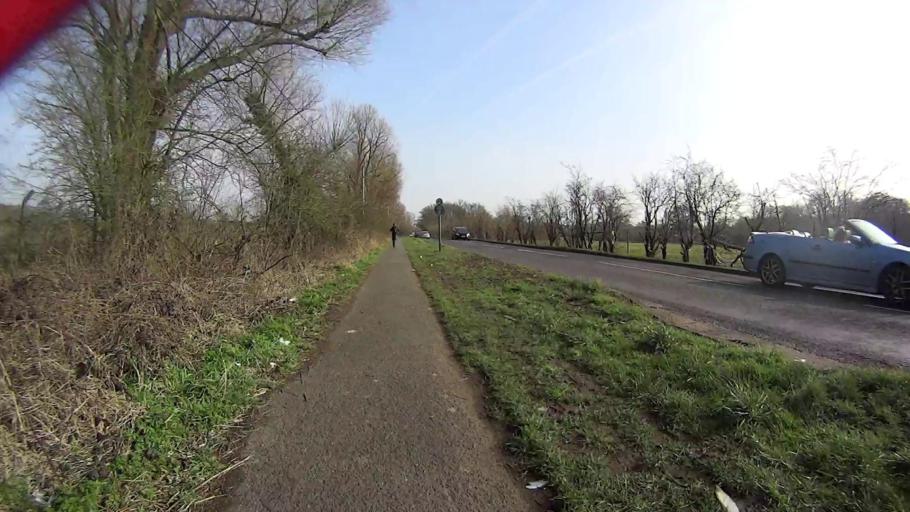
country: GB
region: England
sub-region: Surrey
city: Salfords
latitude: 51.2187
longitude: -0.1810
